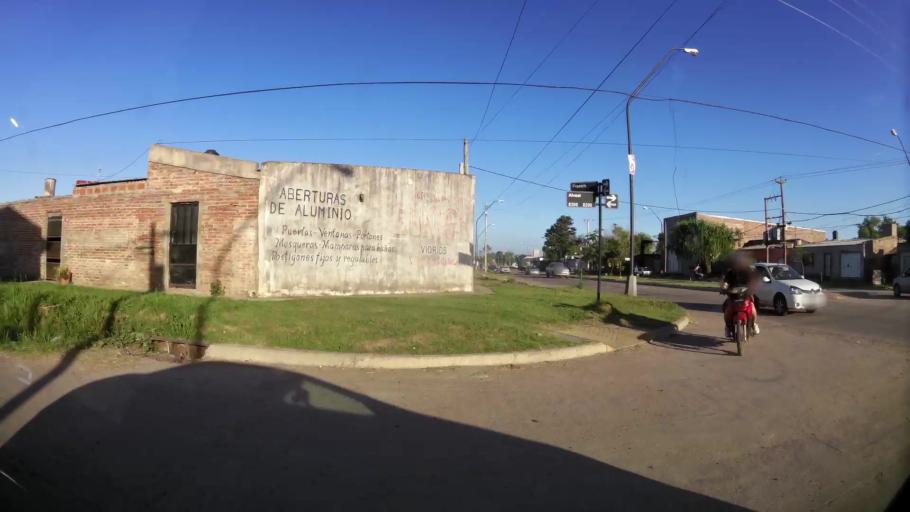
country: AR
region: Santa Fe
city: Santa Fe de la Vera Cruz
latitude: -31.5942
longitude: -60.6839
